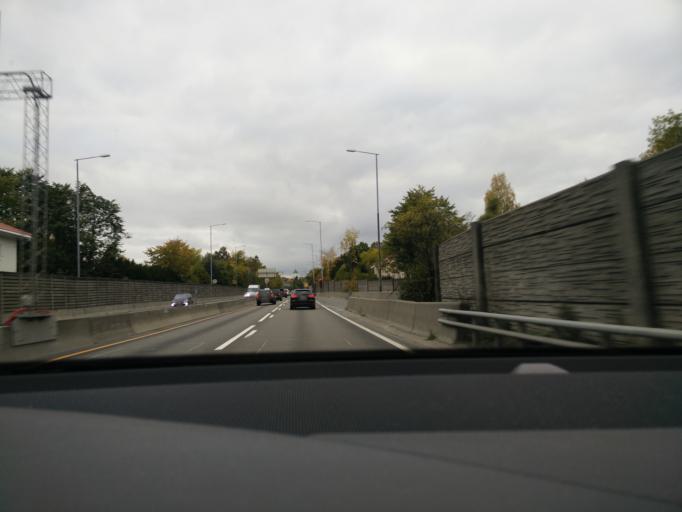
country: NO
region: Oslo
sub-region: Oslo
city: Sjolyststranda
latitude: 59.9338
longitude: 10.6729
